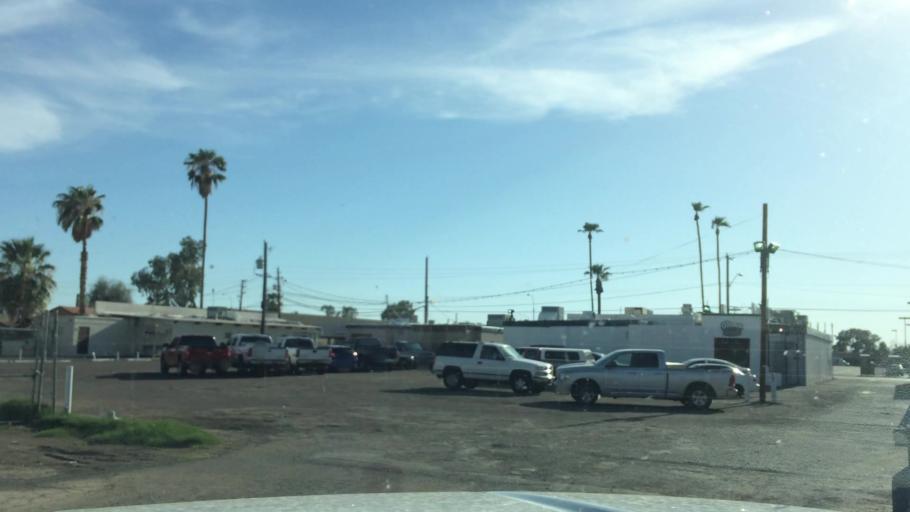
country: US
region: Arizona
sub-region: Maricopa County
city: Glendale
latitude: 33.5525
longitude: -112.1333
